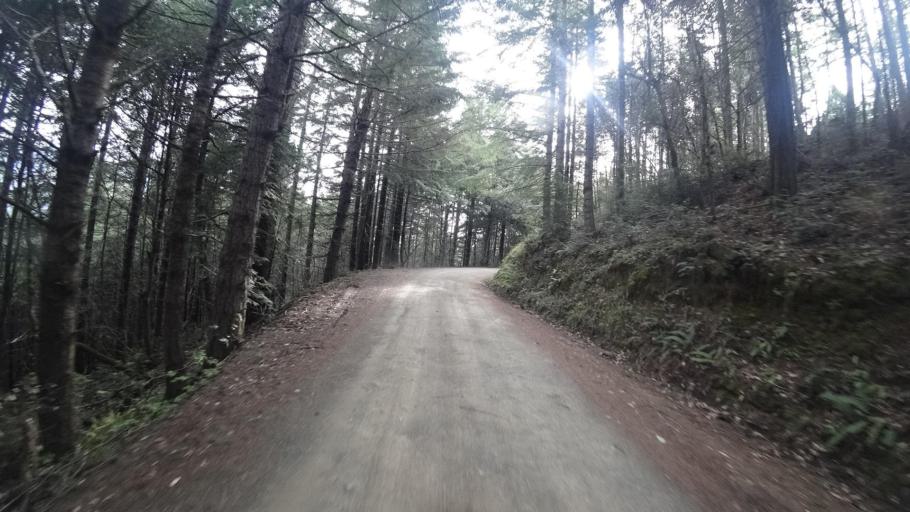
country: US
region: California
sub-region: Humboldt County
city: Redway
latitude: 40.3132
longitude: -123.8229
